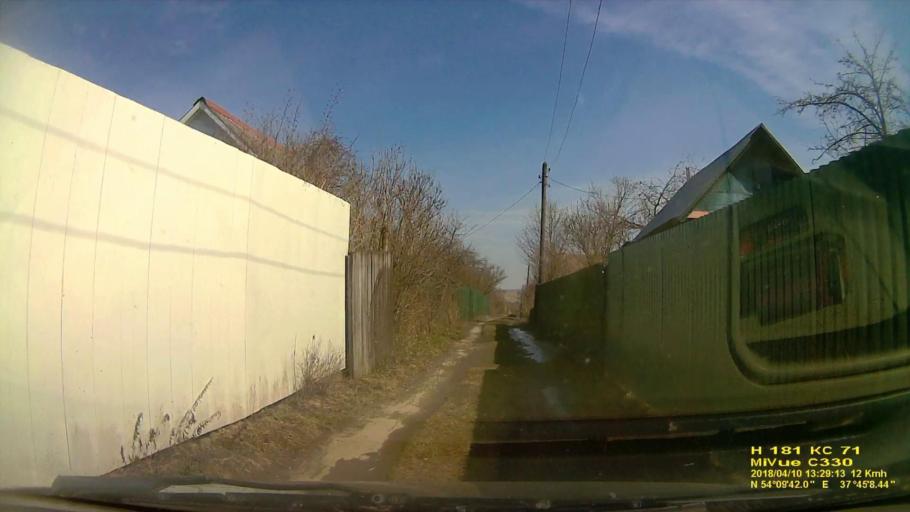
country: RU
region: Tula
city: Bolokhovo
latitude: 54.1616
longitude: 37.7524
